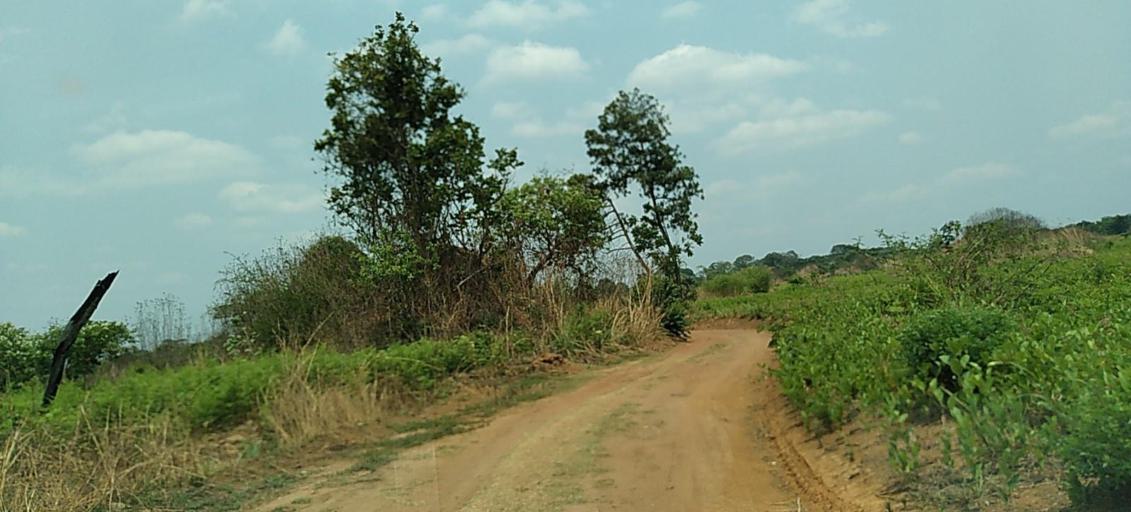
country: ZM
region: Copperbelt
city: Kalulushi
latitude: -12.7587
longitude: 28.0223
